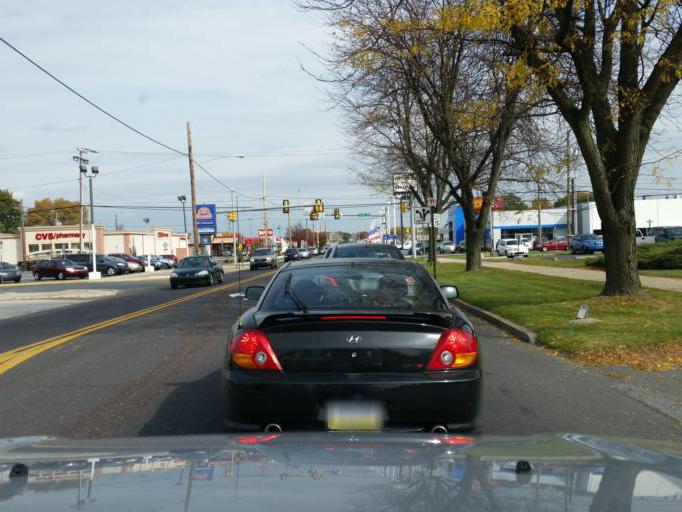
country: US
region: Pennsylvania
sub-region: Lebanon County
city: Palmyra
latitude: 40.3113
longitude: -76.5879
